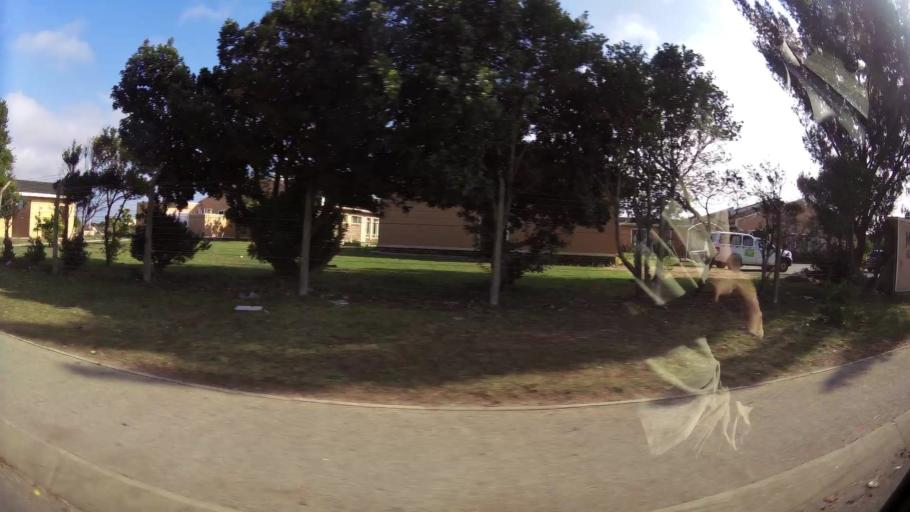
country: ZA
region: Eastern Cape
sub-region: Nelson Mandela Bay Metropolitan Municipality
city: Port Elizabeth
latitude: -33.9200
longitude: 25.5354
